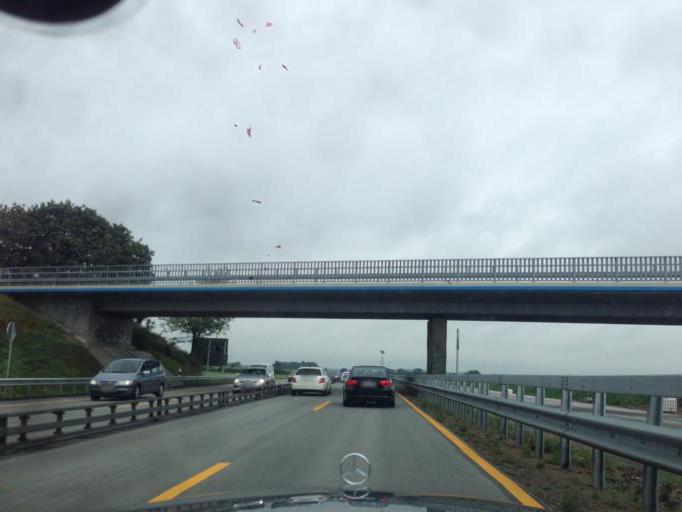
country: DE
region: Schleswig-Holstein
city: Loop
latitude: 54.1466
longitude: 9.9637
